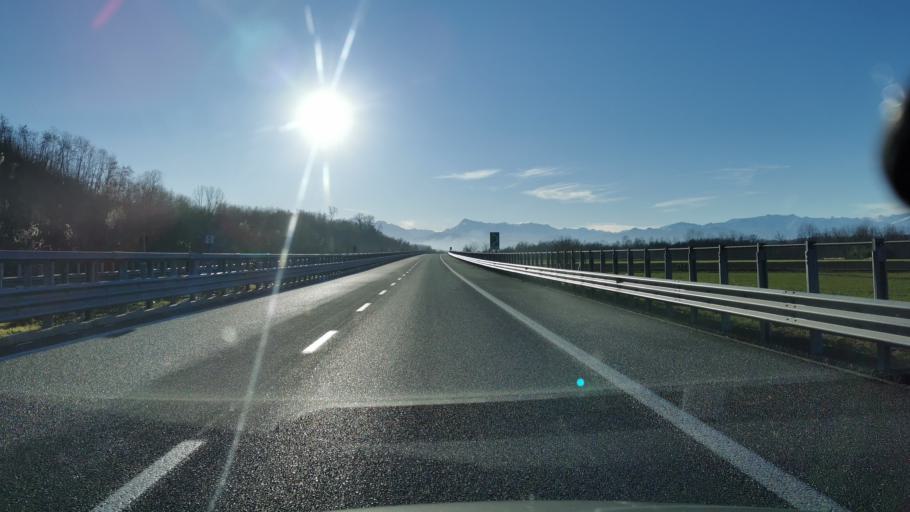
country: IT
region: Piedmont
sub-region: Provincia di Cuneo
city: Montanera
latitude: 44.4559
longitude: 7.6523
